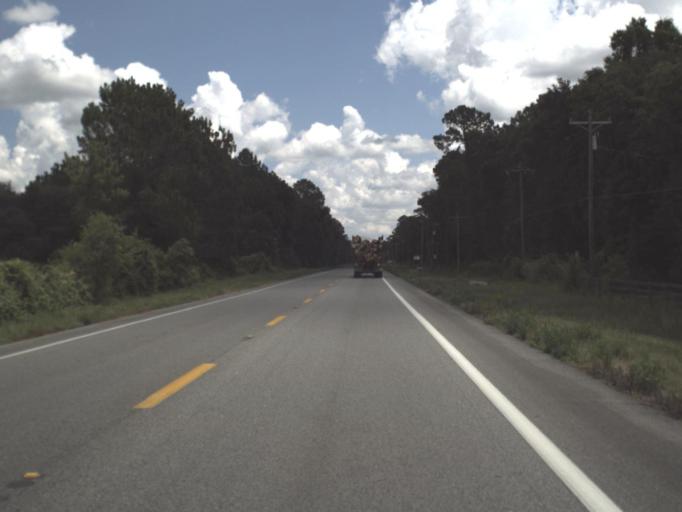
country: US
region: Florida
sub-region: Taylor County
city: Perry
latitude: 30.0951
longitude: -83.6332
